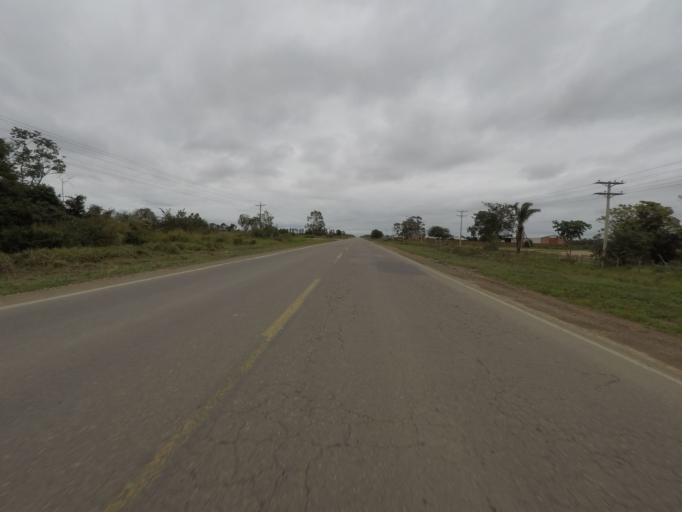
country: BO
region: Santa Cruz
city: Okinawa Numero Uno
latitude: -17.2339
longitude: -62.5554
